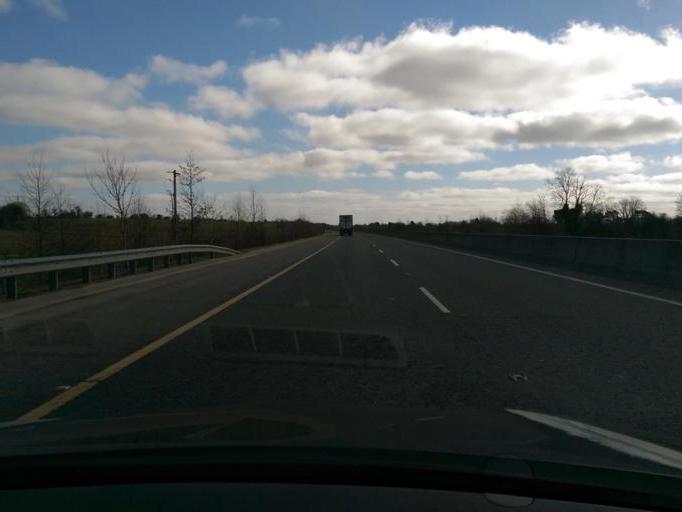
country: IE
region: Leinster
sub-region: An Iarmhi
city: Moate
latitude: 53.3887
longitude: -7.7562
